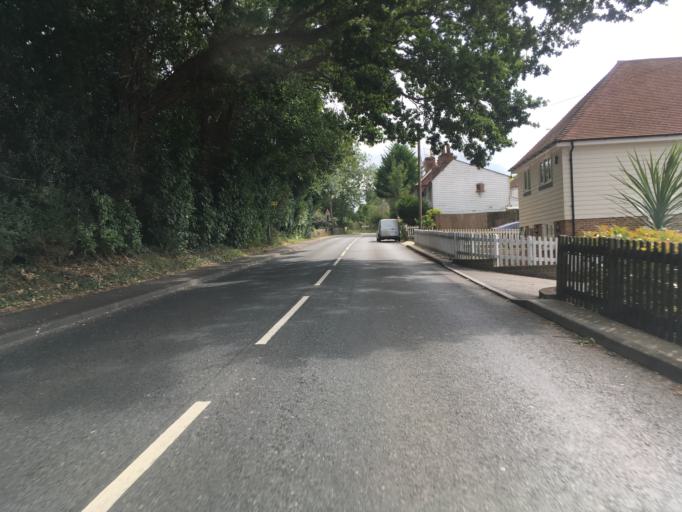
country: GB
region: England
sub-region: Kent
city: Tenterden
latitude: 51.0783
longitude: 0.6953
